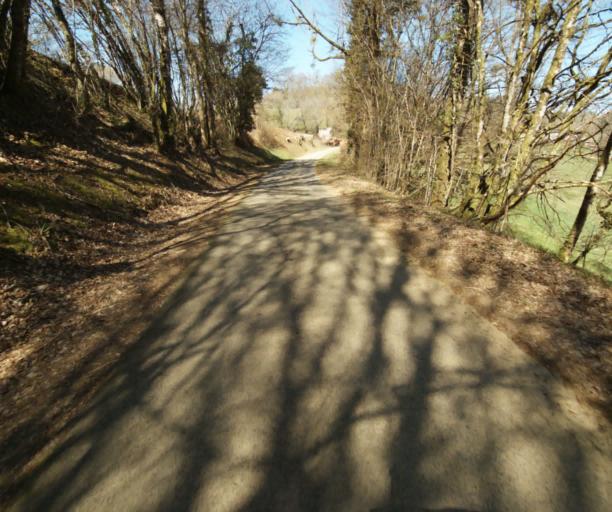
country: FR
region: Limousin
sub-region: Departement de la Correze
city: Saint-Clement
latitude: 45.3192
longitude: 1.7027
